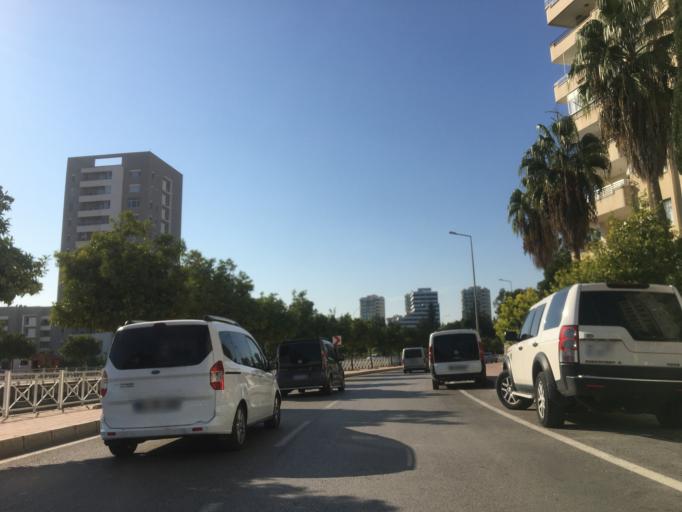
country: TR
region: Adana
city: Seyhan
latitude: 37.0269
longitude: 35.2744
